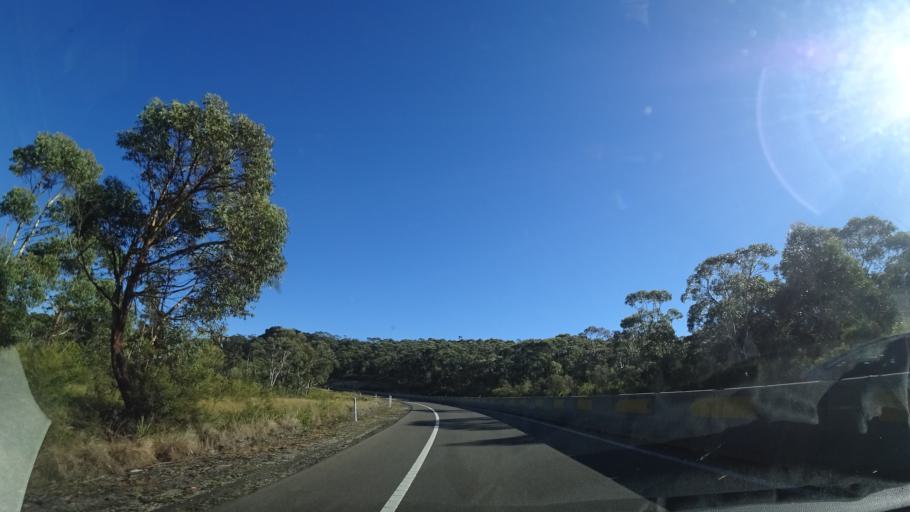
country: AU
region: New South Wales
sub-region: Blue Mountains Municipality
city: Blackheath
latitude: -33.5270
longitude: 150.3102
